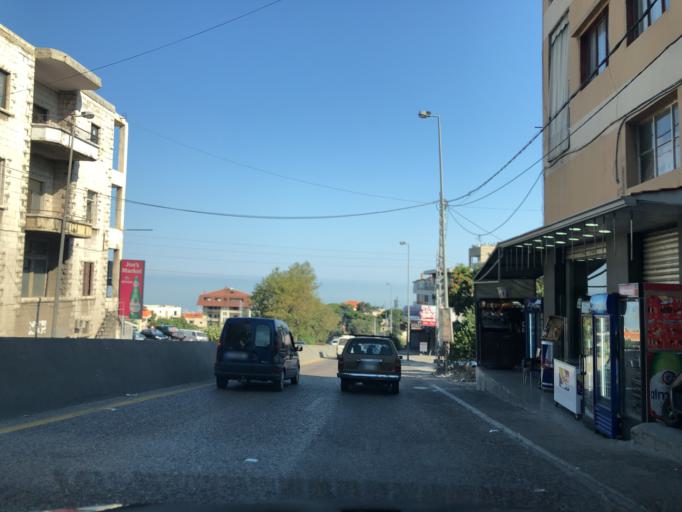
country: LB
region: Mont-Liban
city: Aaley
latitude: 33.8167
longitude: 35.6076
